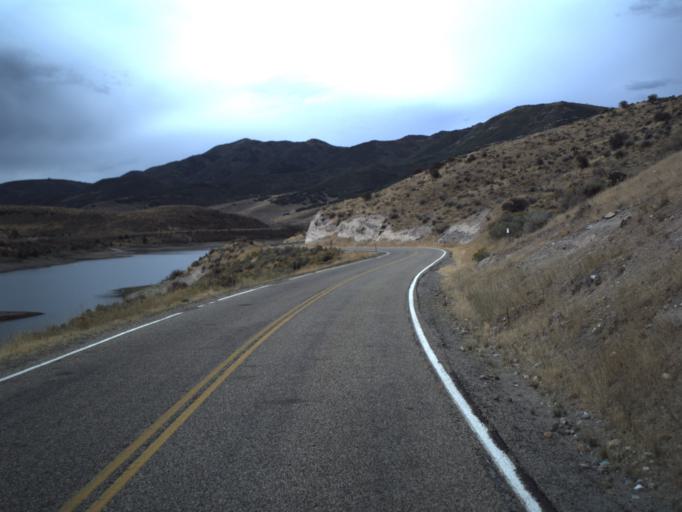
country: US
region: Utah
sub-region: Morgan County
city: Morgan
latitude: 40.9233
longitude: -111.5759
